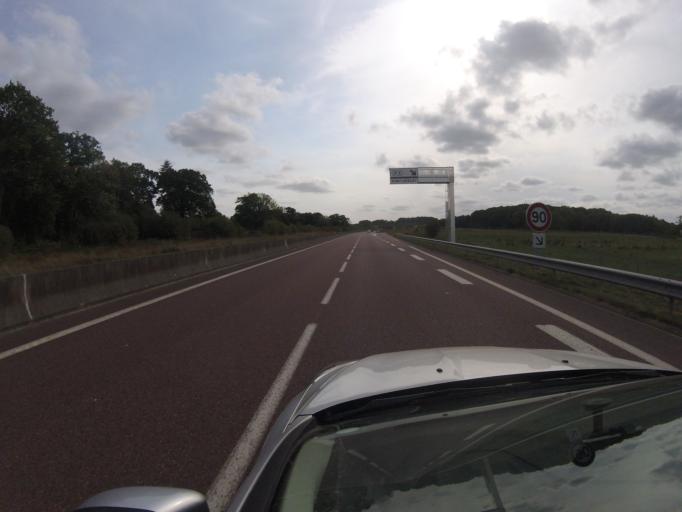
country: FR
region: Lower Normandy
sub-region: Departement de la Manche
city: Pont-Hebert
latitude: 49.1933
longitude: -1.1322
